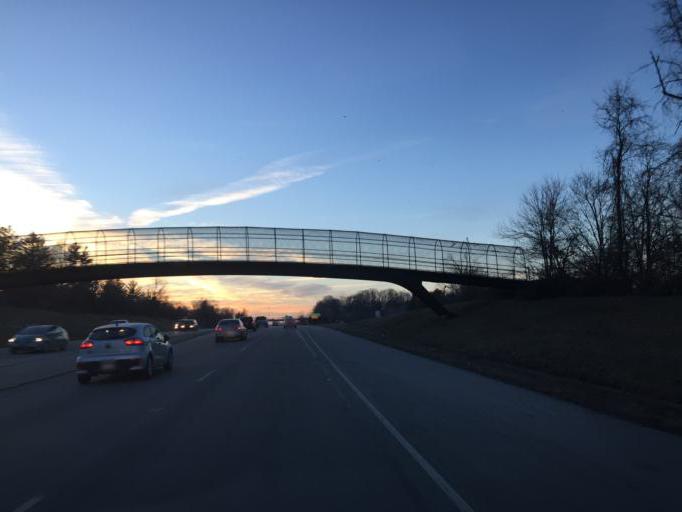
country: US
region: Indiana
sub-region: Monroe County
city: Bloomington
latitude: 39.1868
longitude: -86.5429
